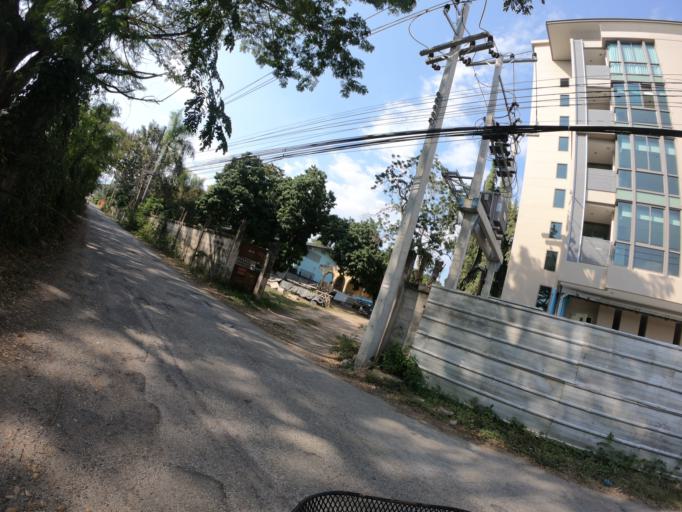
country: TH
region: Chiang Mai
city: Chiang Mai
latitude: 18.7928
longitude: 99.0173
